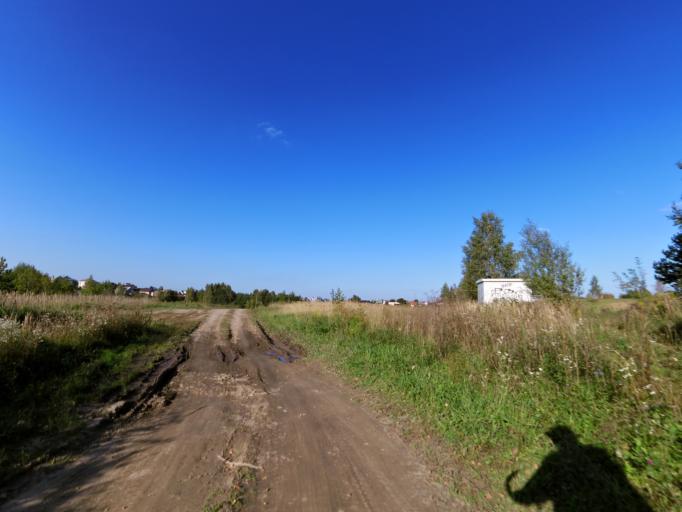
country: LT
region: Vilnius County
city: Pilaite
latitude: 54.7195
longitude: 25.1818
